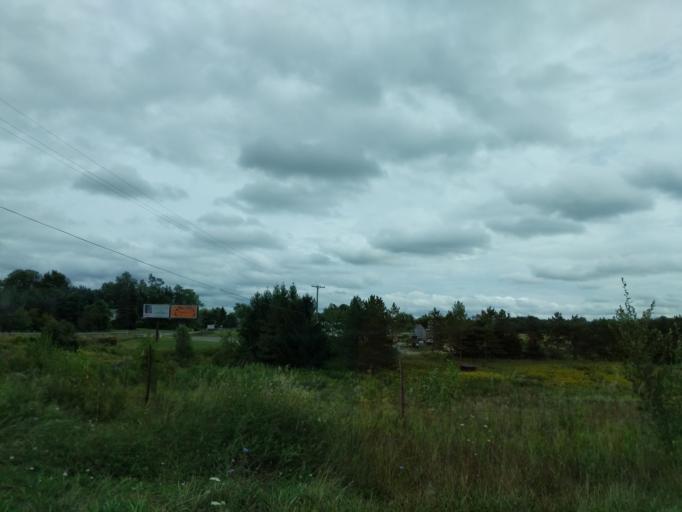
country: US
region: Michigan
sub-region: Lapeer County
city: Barnes Lake-Millers Lake
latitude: 43.3362
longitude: -83.3428
